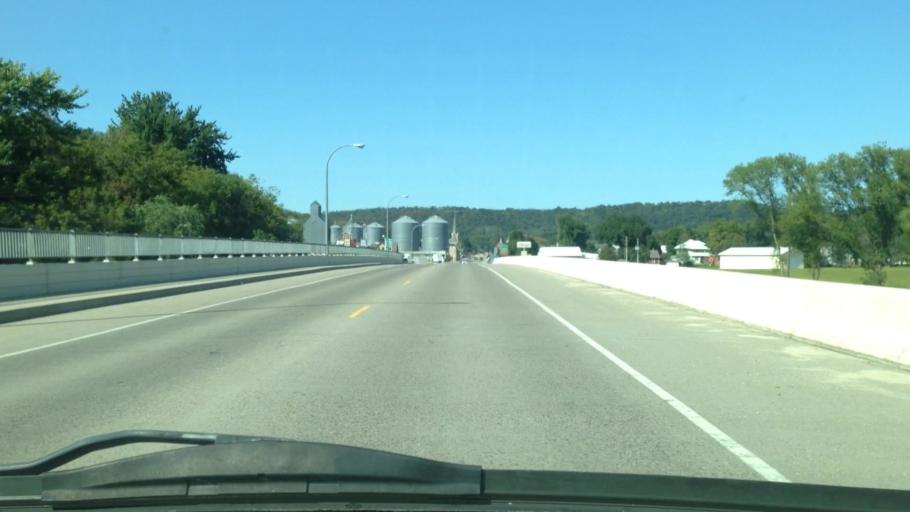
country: US
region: Minnesota
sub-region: Fillmore County
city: Rushford
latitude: 43.8028
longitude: -91.7531
